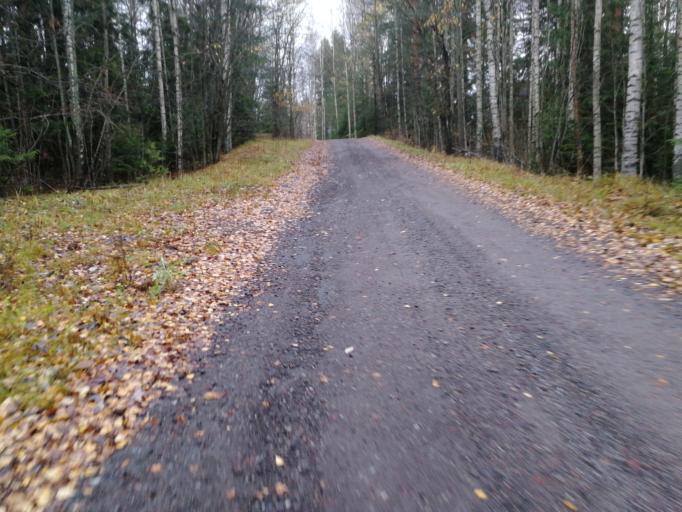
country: FI
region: Pirkanmaa
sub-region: Tampere
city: Tampere
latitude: 61.4560
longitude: 23.8703
